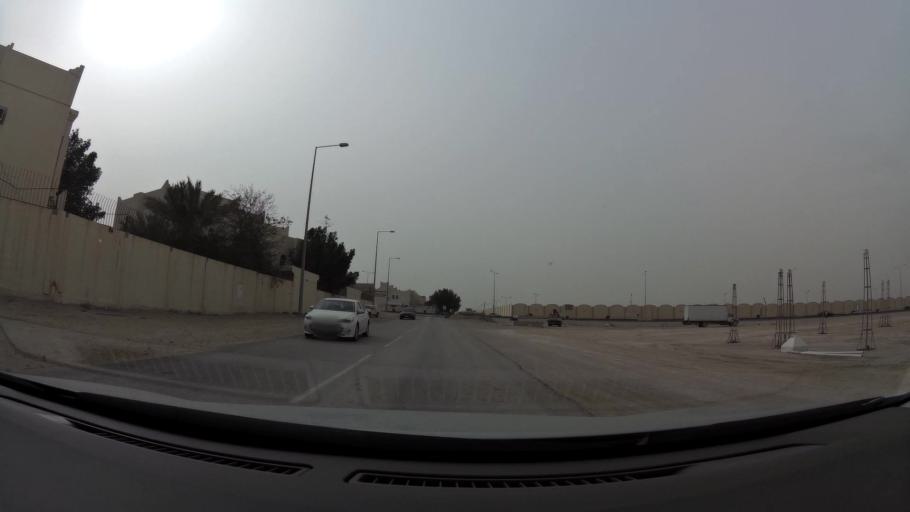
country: QA
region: Baladiyat ad Dawhah
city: Doha
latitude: 25.2531
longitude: 51.4922
